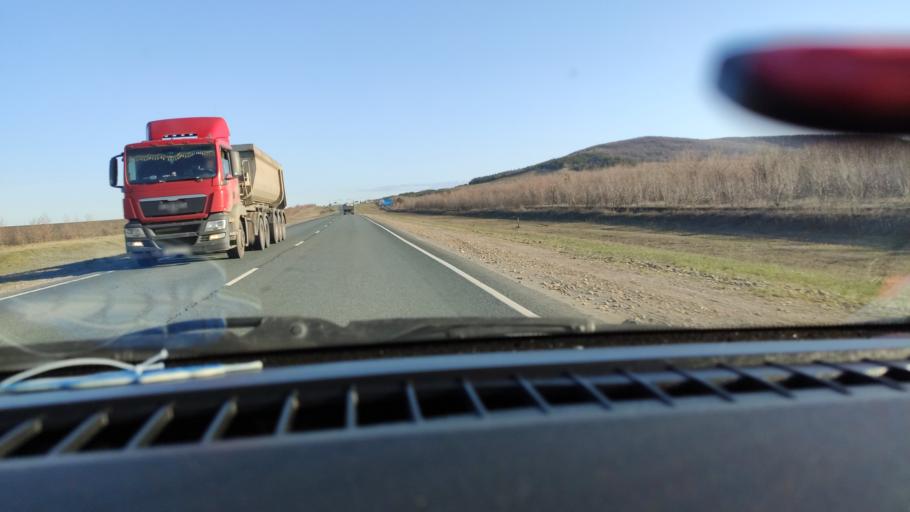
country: RU
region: Saratov
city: Alekseyevka
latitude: 52.2854
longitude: 47.9310
